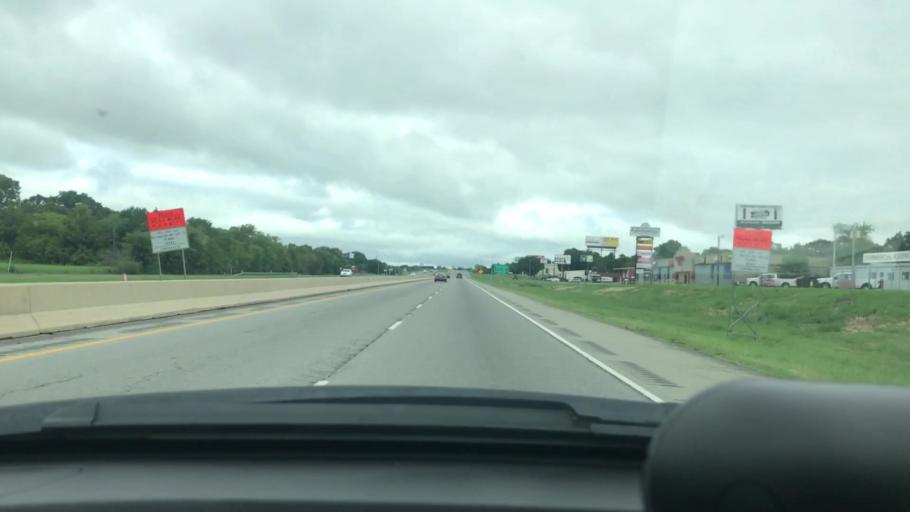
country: US
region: Texas
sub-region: Grayson County
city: Sherman
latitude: 33.6219
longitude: -96.6115
